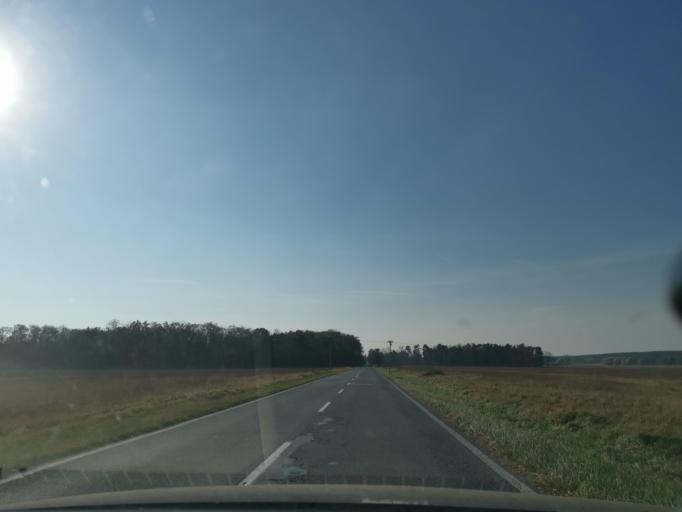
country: SK
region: Trnavsky
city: Gbely
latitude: 48.5754
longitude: 17.1716
